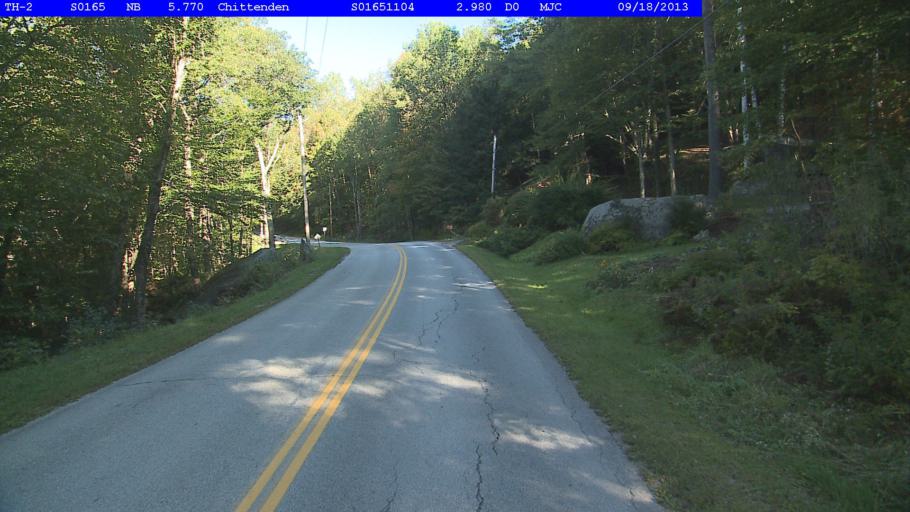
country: US
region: Vermont
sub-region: Rutland County
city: Rutland
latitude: 43.7184
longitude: -72.9633
